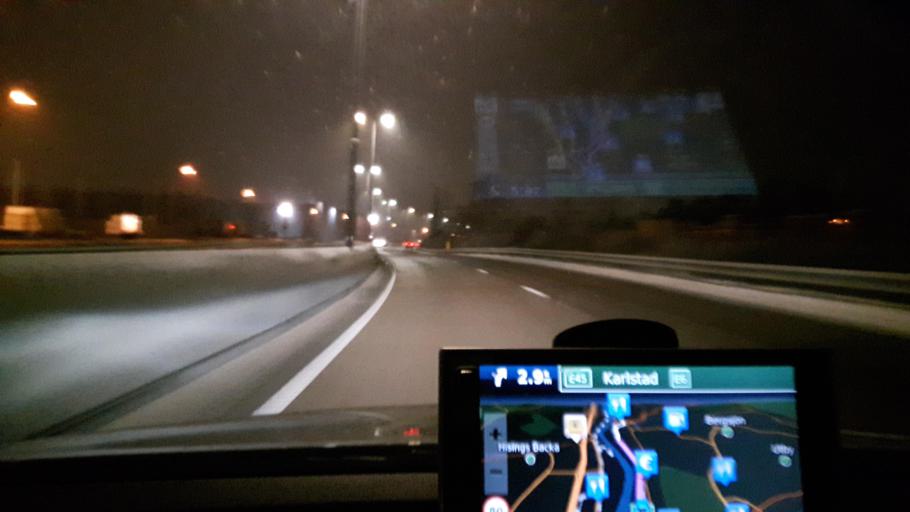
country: SE
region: Vaestra Goetaland
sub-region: Goteborg
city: Goeteborg
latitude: 57.7372
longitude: 12.0035
